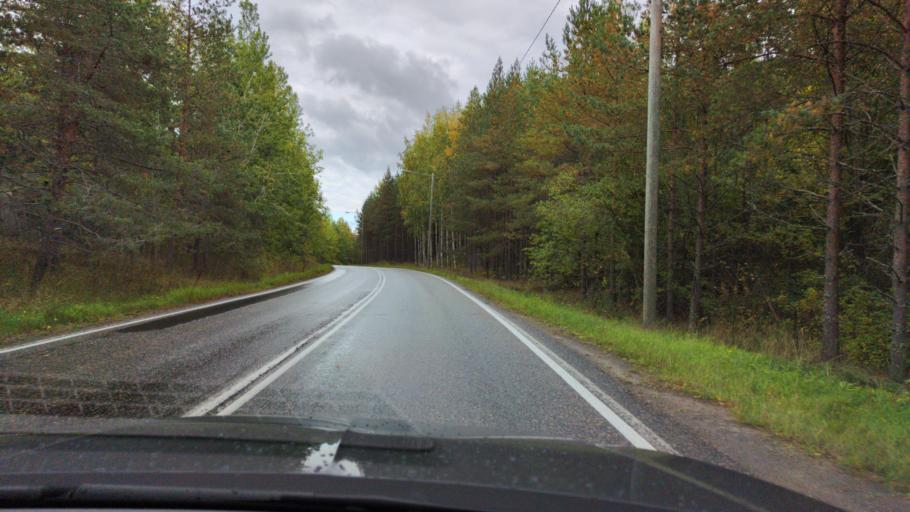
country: FI
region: Varsinais-Suomi
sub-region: Turku
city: Turku
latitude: 60.3671
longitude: 22.2186
